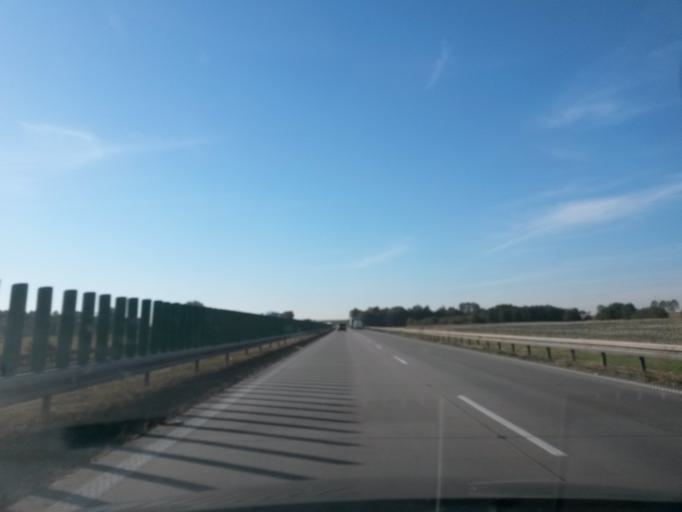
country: PL
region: Lower Silesian Voivodeship
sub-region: Powiat wroclawski
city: Katy Wroclawskie
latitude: 51.0263
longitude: 16.6671
